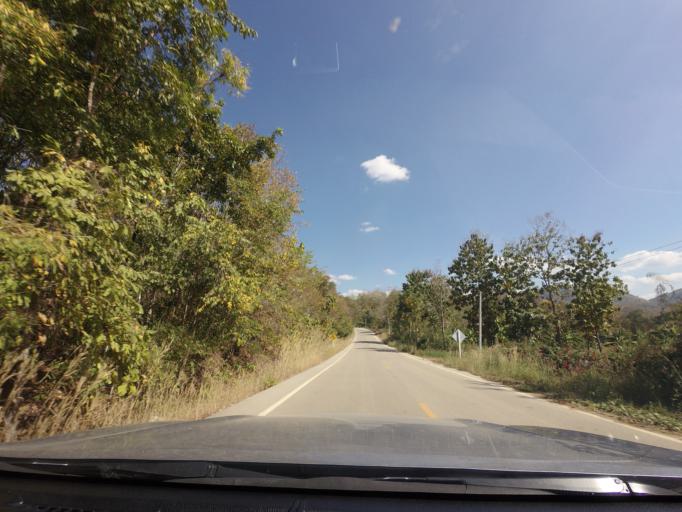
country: TH
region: Lampang
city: Chae Hom
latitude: 18.6033
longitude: 99.6214
